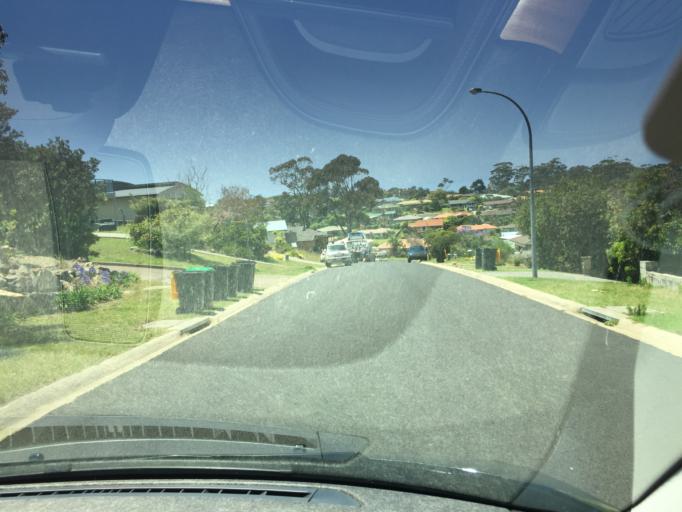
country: AU
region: New South Wales
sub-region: Bega Valley
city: Merimbula
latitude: -36.8538
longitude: 149.9300
